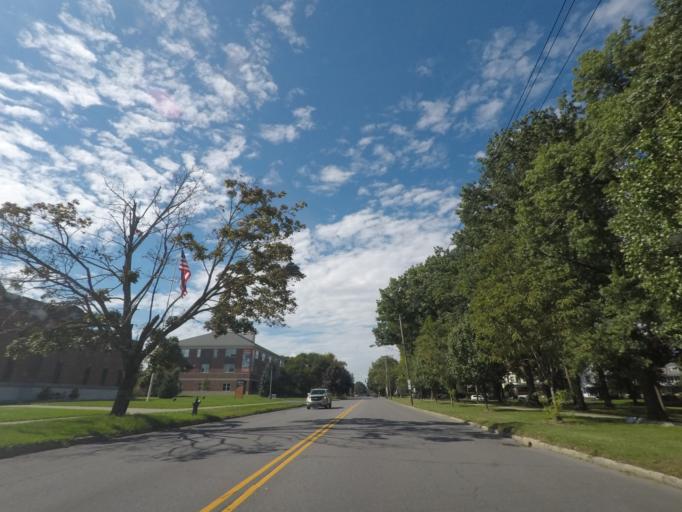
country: US
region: New York
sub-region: Albany County
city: Albany
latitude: 42.6527
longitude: -73.7811
